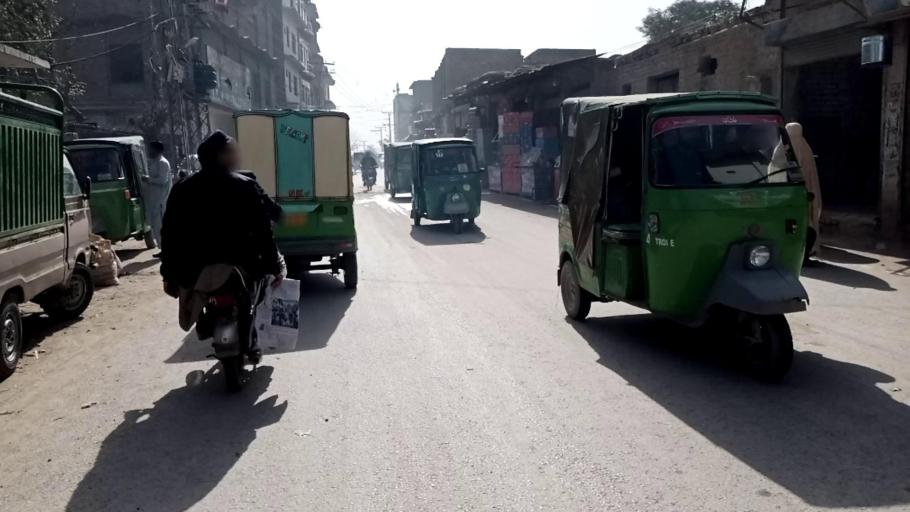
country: PK
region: Khyber Pakhtunkhwa
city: Peshawar
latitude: 34.0023
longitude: 71.5857
